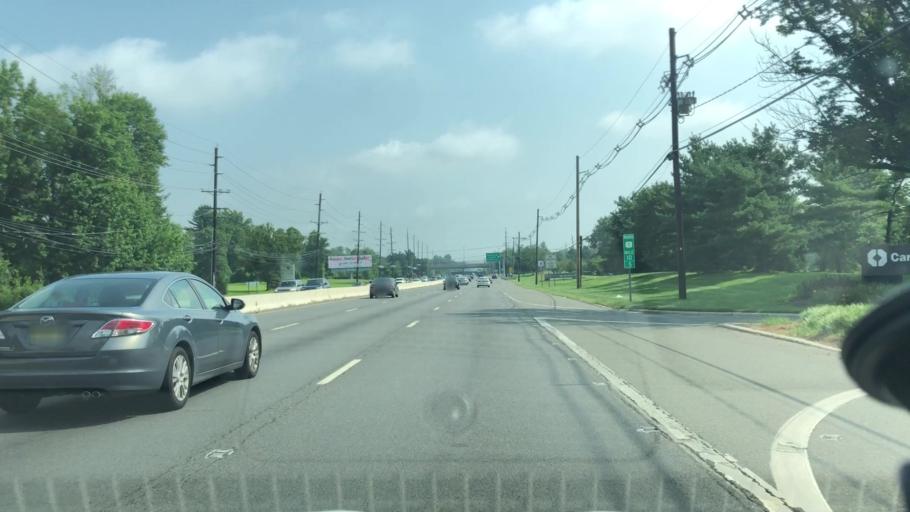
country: US
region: New Jersey
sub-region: Mercer County
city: Princeton
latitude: 40.3233
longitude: -74.6477
